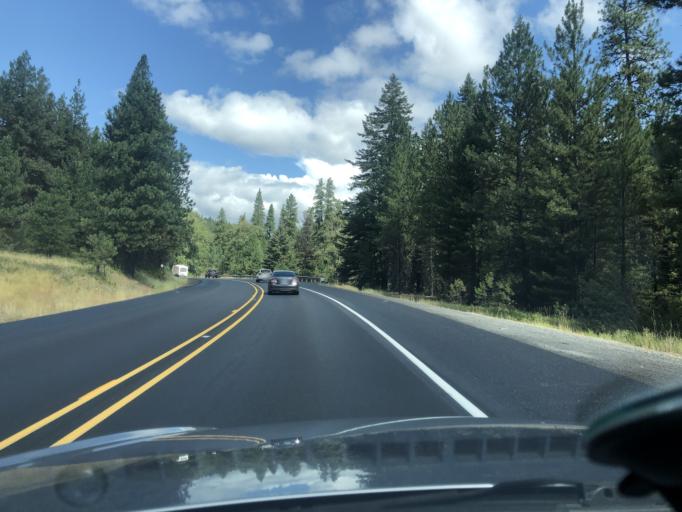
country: US
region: Washington
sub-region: Kittitas County
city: Cle Elum
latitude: 47.2942
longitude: -120.7001
